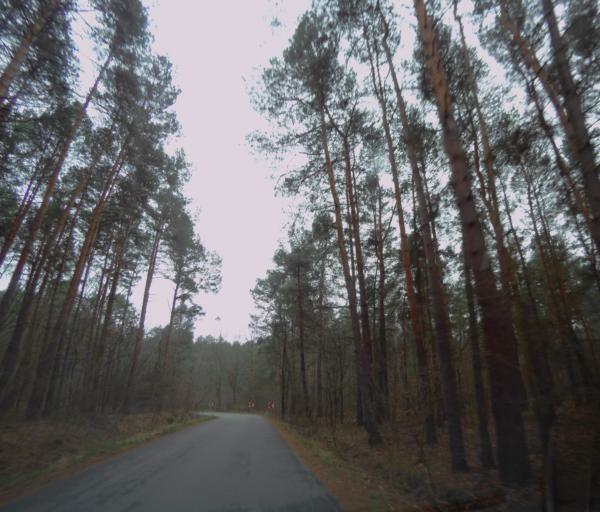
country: PL
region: Subcarpathian Voivodeship
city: Nowa Sarzyna
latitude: 50.3102
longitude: 22.3418
